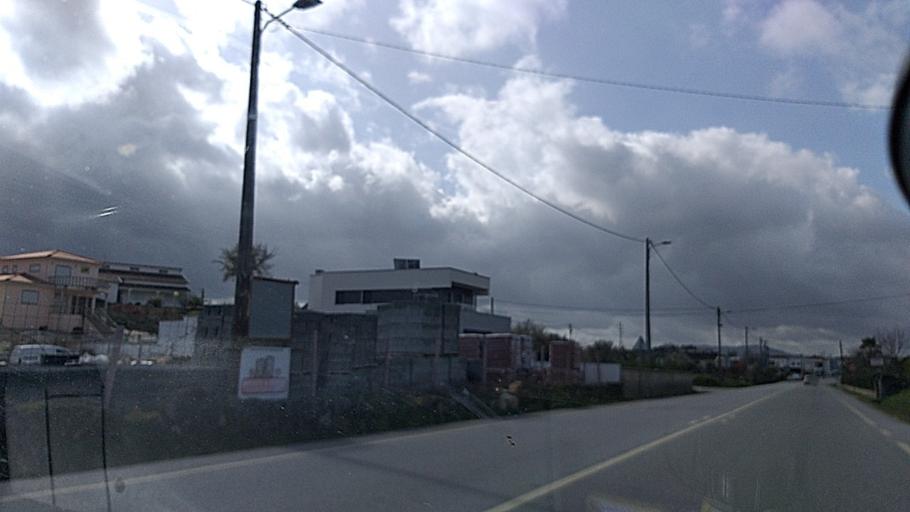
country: PT
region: Viseu
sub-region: Satao
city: Satao
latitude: 40.6683
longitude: -7.7116
